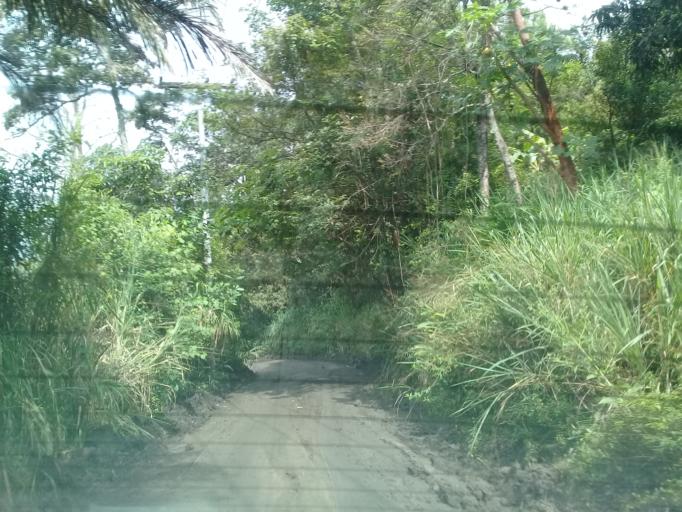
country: CO
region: Cundinamarca
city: Quipile
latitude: 4.6865
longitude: -74.5381
